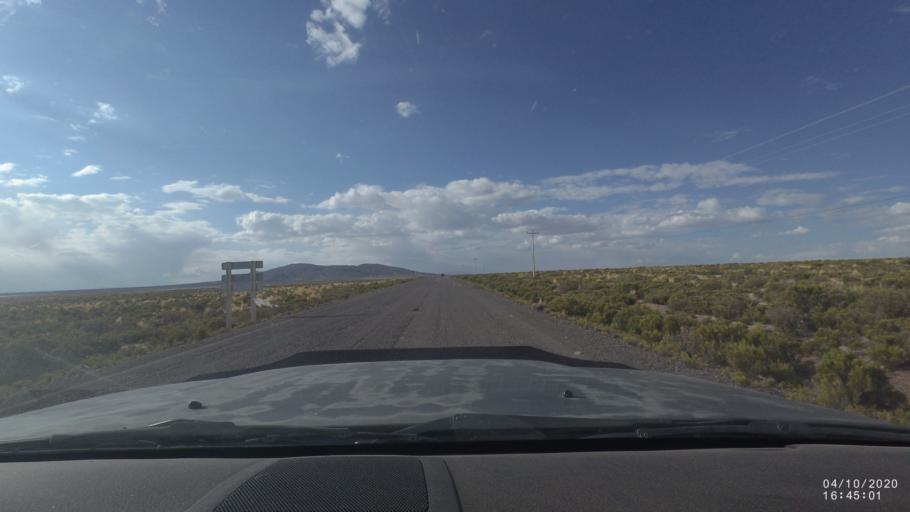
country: BO
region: Oruro
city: Poopo
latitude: -18.6754
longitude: -67.5613
